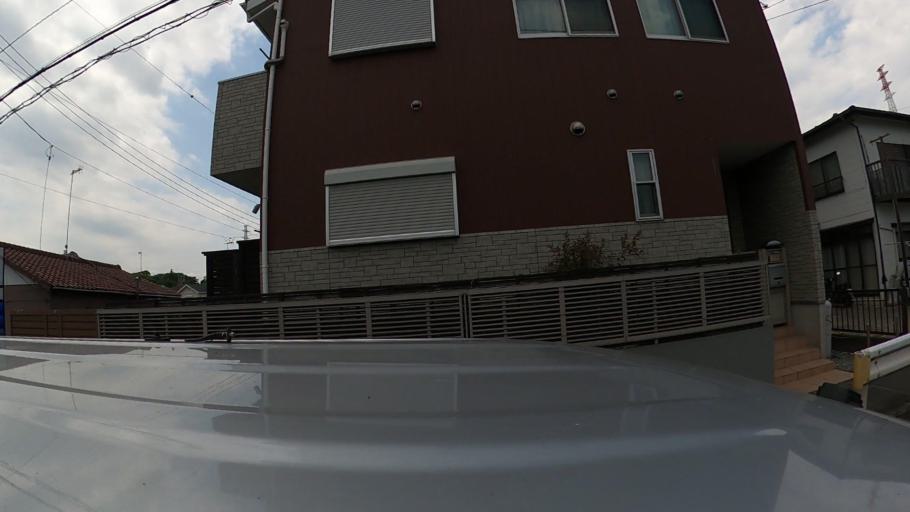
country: JP
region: Kanagawa
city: Chigasaki
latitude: 35.3713
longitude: 139.3902
